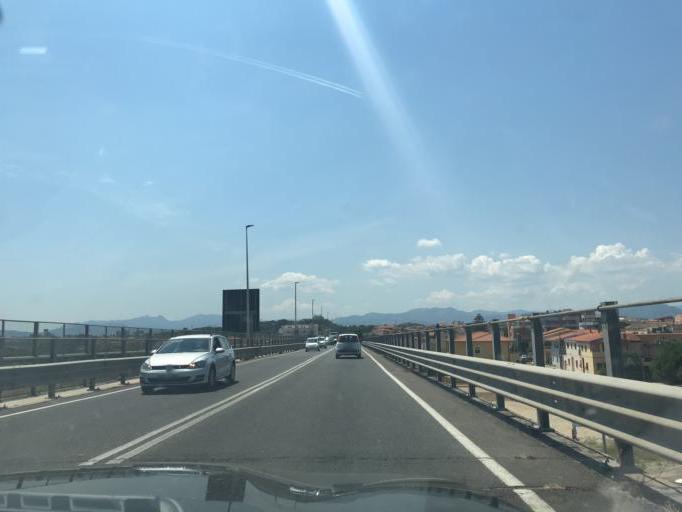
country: IT
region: Sardinia
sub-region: Provincia di Olbia-Tempio
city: Olbia
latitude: 40.9182
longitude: 9.5014
